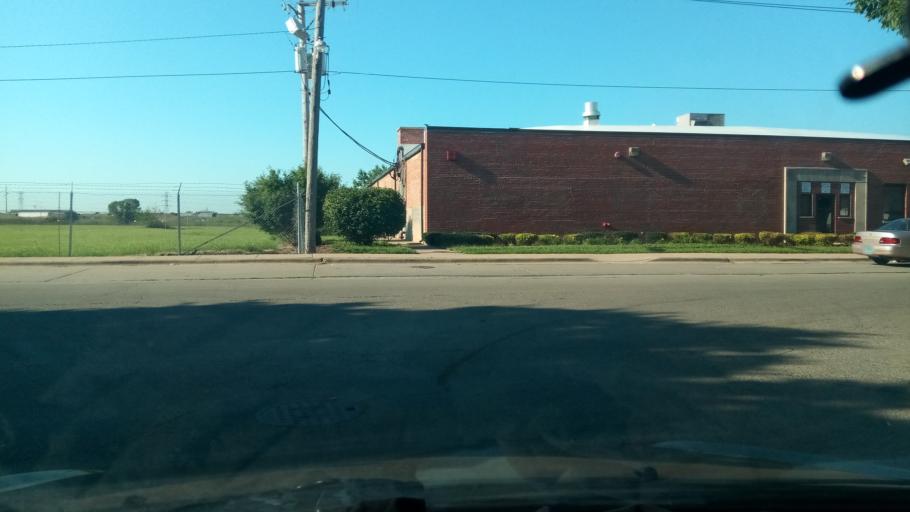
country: US
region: Illinois
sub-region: Cook County
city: Hometown
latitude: 41.7684
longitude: -87.7297
